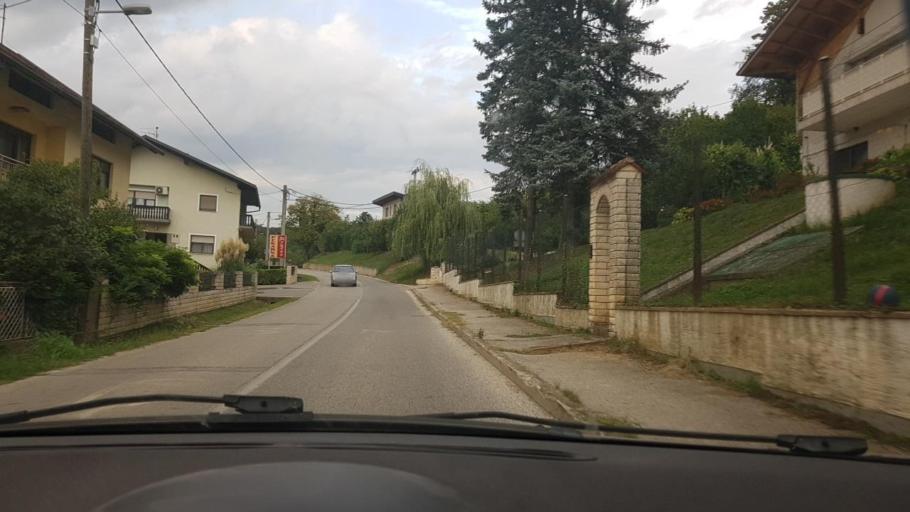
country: HR
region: Grad Zagreb
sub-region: Sesvete
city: Sesvete
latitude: 45.9107
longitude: 16.1665
